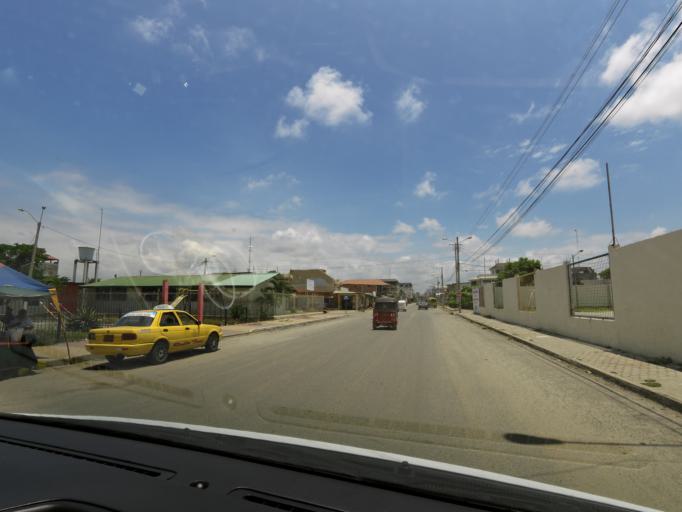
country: EC
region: El Oro
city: Huaquillas
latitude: -3.4763
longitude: -80.2366
